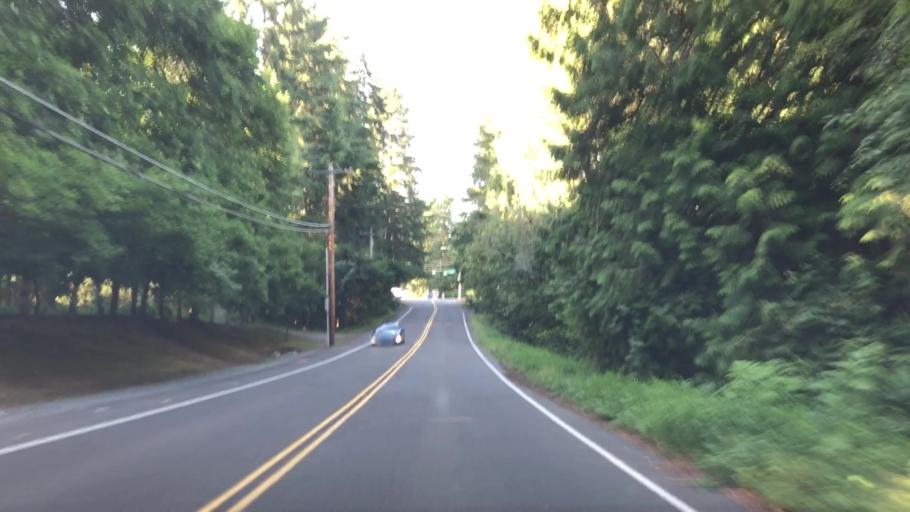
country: US
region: Washington
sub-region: King County
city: Woodinville
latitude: 47.7600
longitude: -122.1262
